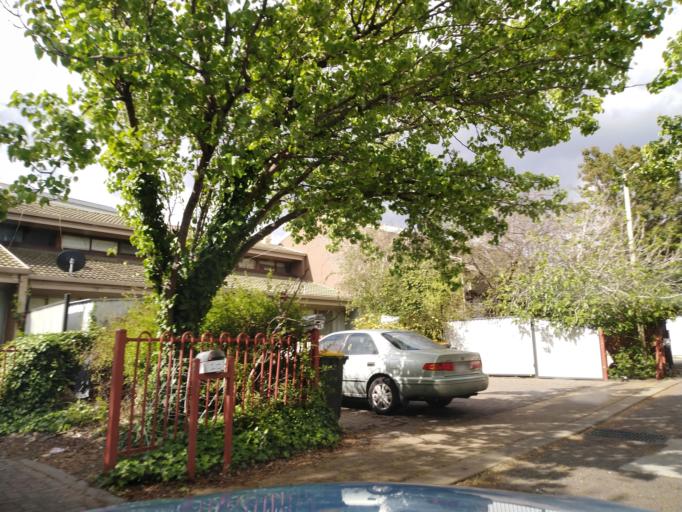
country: AU
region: Victoria
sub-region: Hobsons Bay
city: South Kingsville
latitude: -37.8410
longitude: 144.8619
